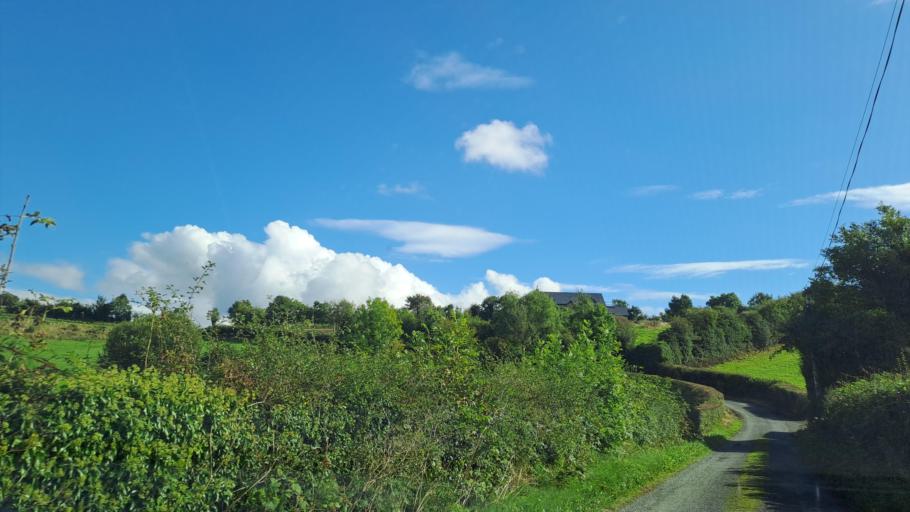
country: IE
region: Ulster
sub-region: An Cabhan
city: Kingscourt
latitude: 53.9965
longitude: -6.8734
